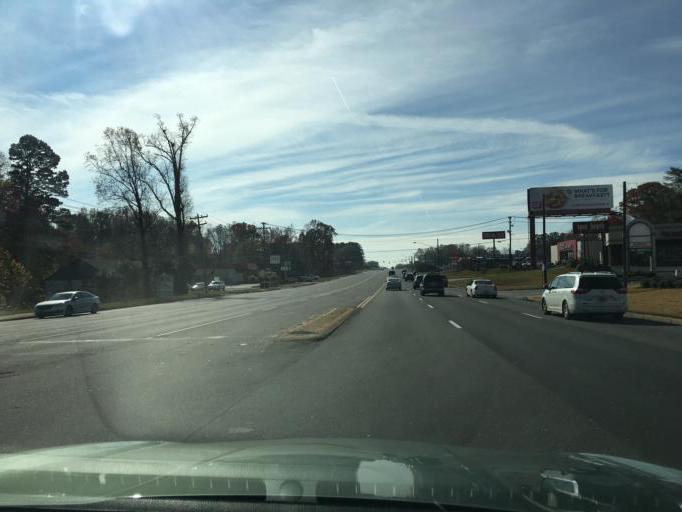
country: US
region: South Carolina
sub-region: Greenville County
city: Wade Hampton
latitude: 34.9005
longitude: -82.3368
